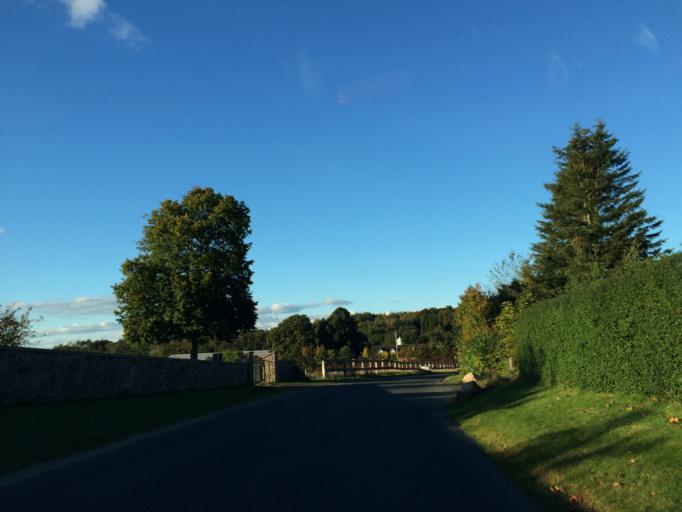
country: DK
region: Central Jutland
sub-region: Silkeborg Kommune
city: Svejbaek
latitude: 56.1561
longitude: 9.6914
